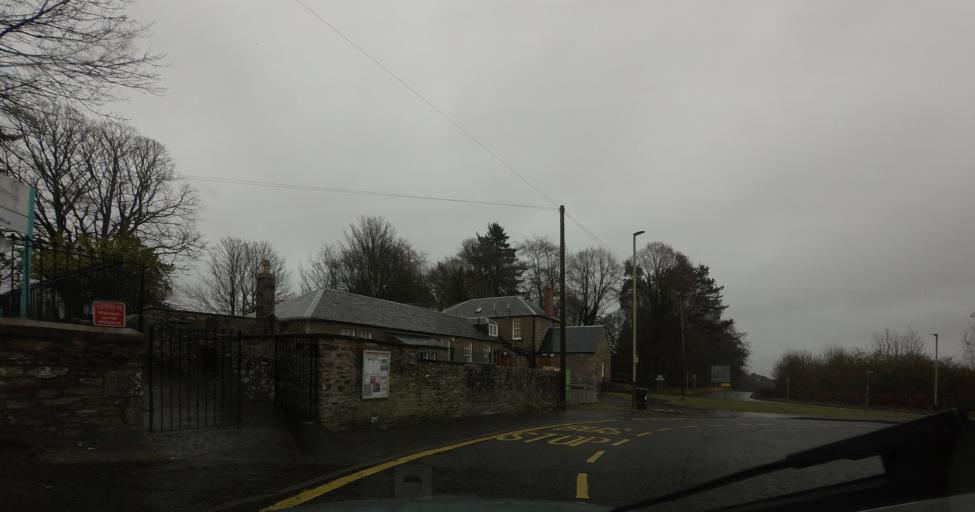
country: GB
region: Scotland
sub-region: Angus
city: Muirhead
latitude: 56.4846
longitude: -3.0748
